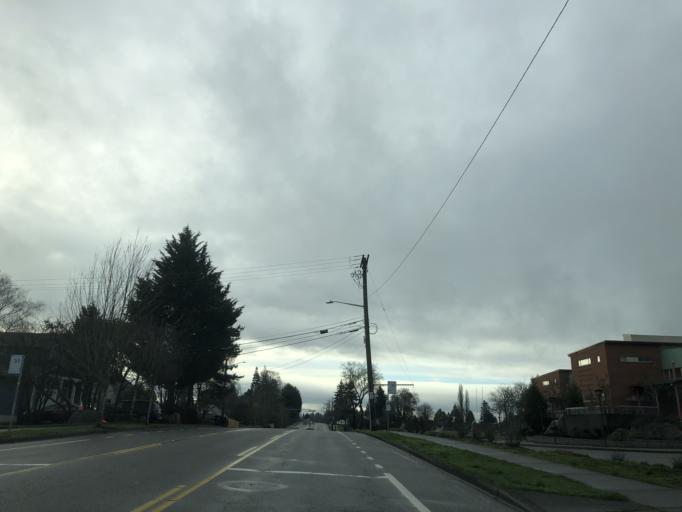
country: US
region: Washington
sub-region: Pierce County
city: Tacoma
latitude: 47.2124
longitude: -122.4582
